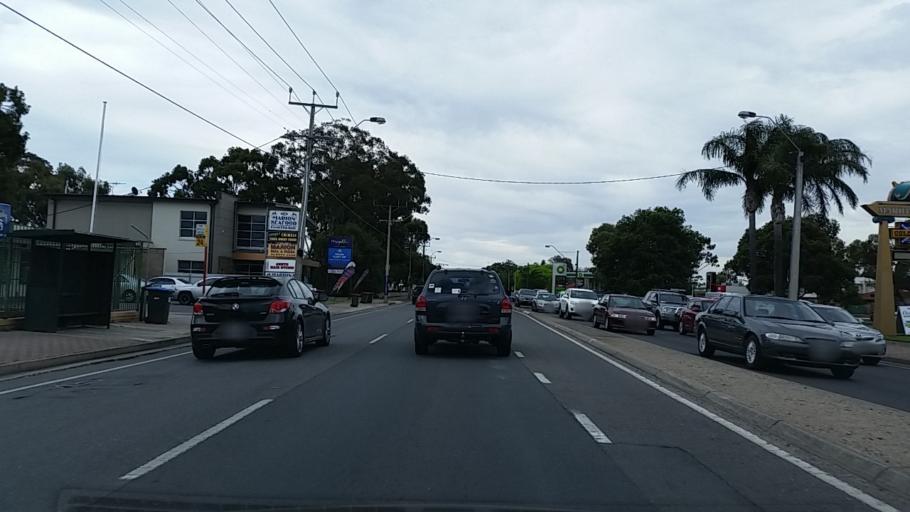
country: AU
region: South Australia
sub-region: Marion
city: Clovelly Park
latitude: -35.0040
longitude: 138.5578
